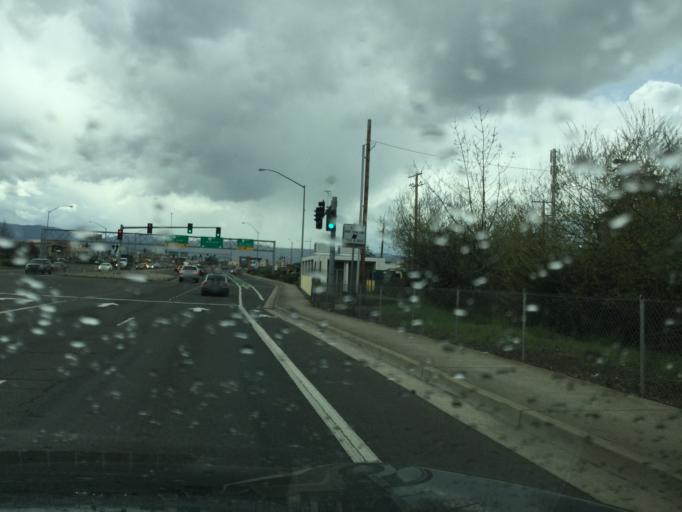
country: US
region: Oregon
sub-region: Jackson County
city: Medford
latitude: 42.3476
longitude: -122.8798
